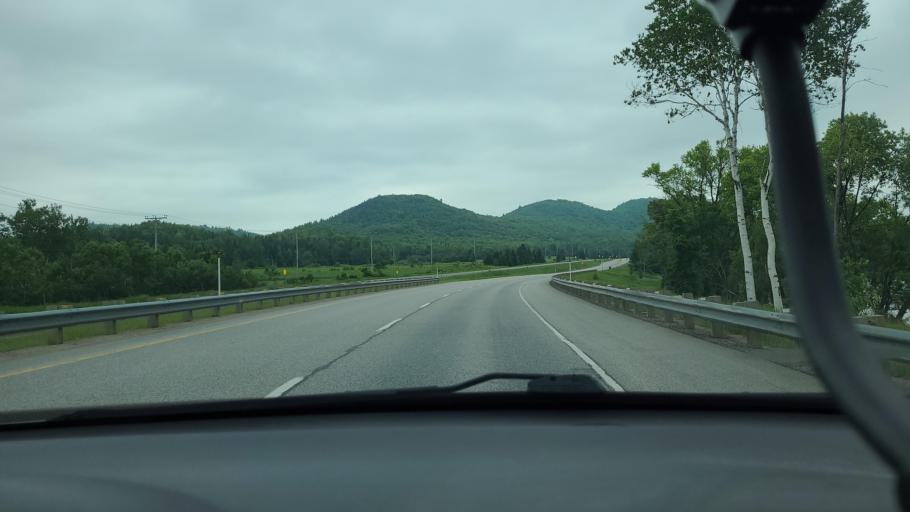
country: CA
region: Quebec
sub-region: Laurentides
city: Labelle
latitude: 46.1856
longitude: -74.7303
